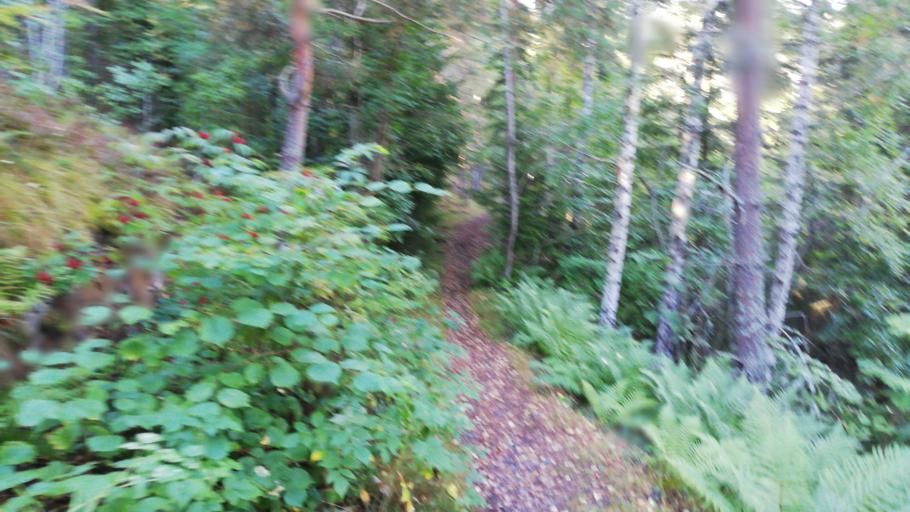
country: NO
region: Buskerud
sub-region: Drammen
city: Drammen
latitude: 59.7580
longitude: 10.1725
